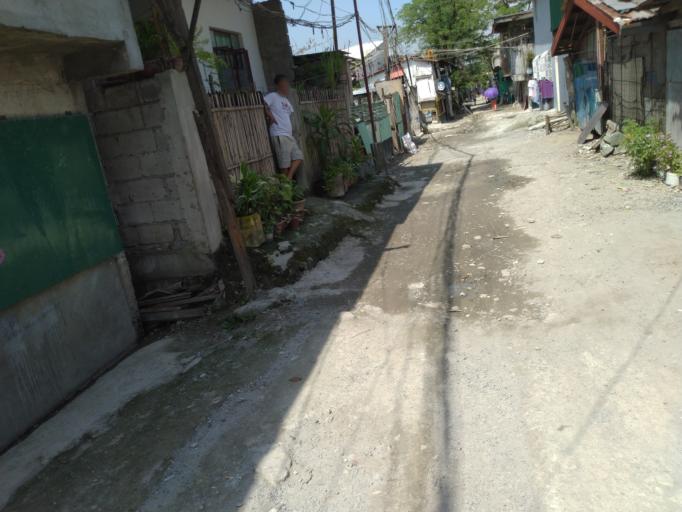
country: PH
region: Calabarzon
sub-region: Province of Rizal
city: Taytay
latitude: 14.5397
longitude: 121.1128
